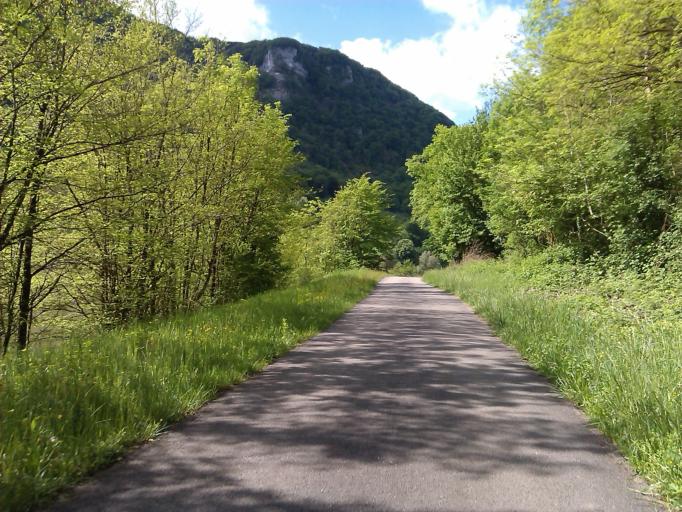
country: FR
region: Franche-Comte
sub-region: Departement du Doubs
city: Roulans
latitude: 47.3242
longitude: 6.2854
